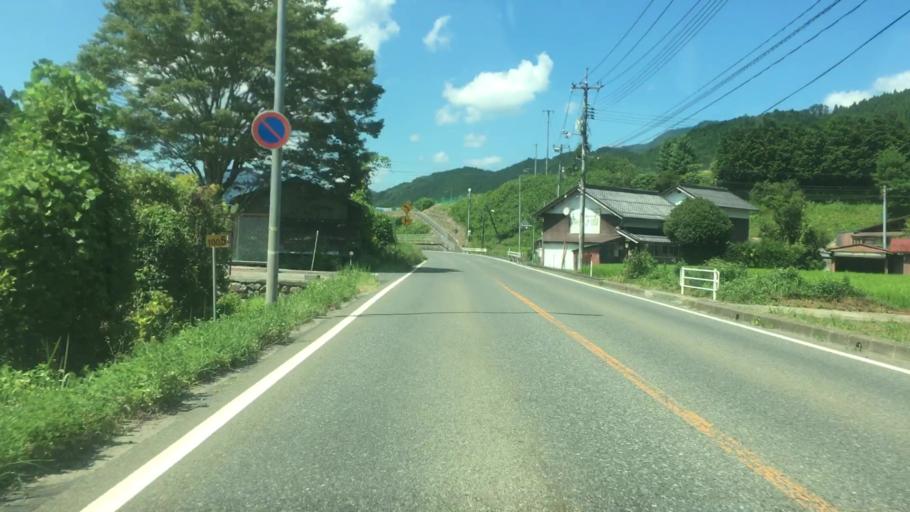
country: JP
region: Tottori
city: Tottori
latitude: 35.2427
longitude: 134.2294
